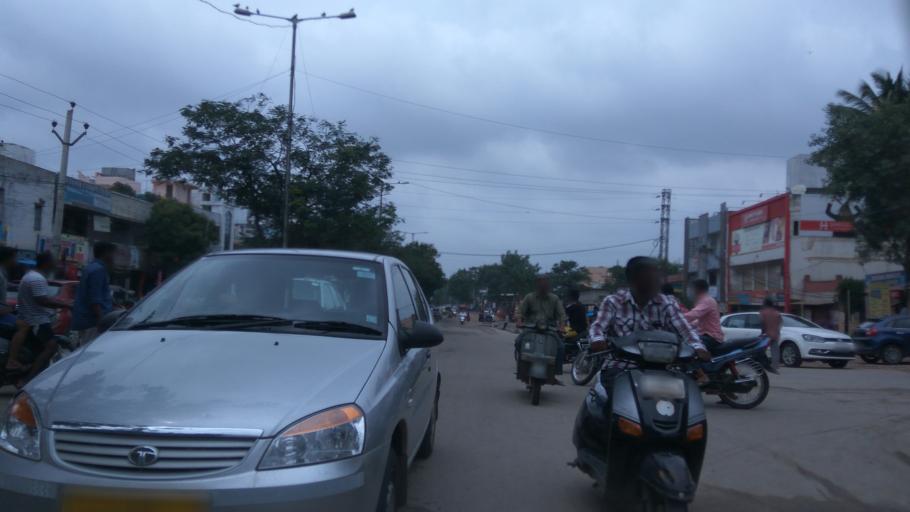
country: IN
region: Telangana
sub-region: Rangareddi
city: Secunderabad
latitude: 17.4824
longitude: 78.5378
